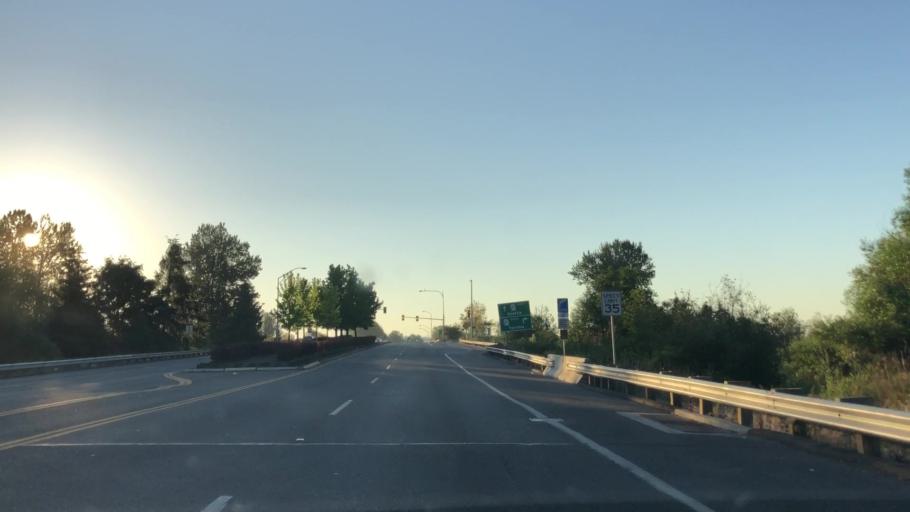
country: US
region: Washington
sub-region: King County
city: Auburn
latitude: 47.3224
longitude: -122.2487
